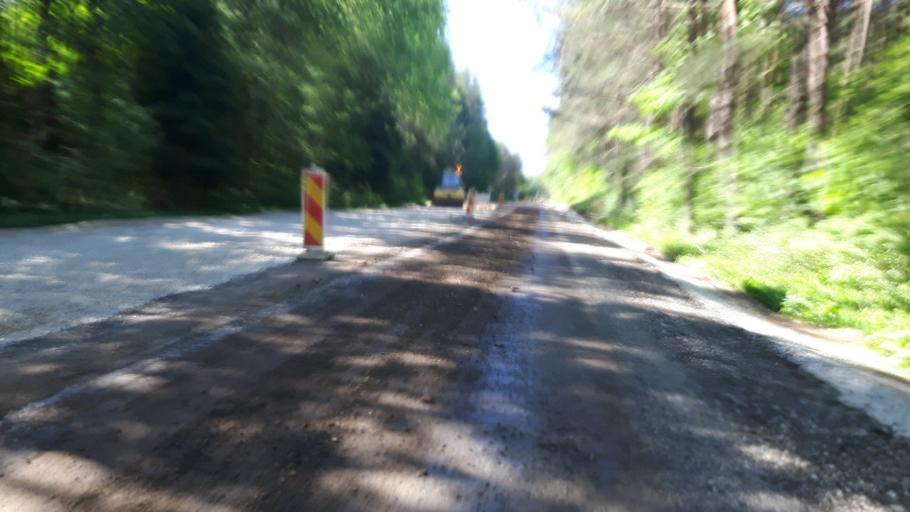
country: EE
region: Ida-Virumaa
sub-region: Narva-Joesuu linn
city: Narva-Joesuu
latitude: 59.4217
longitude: 27.9783
